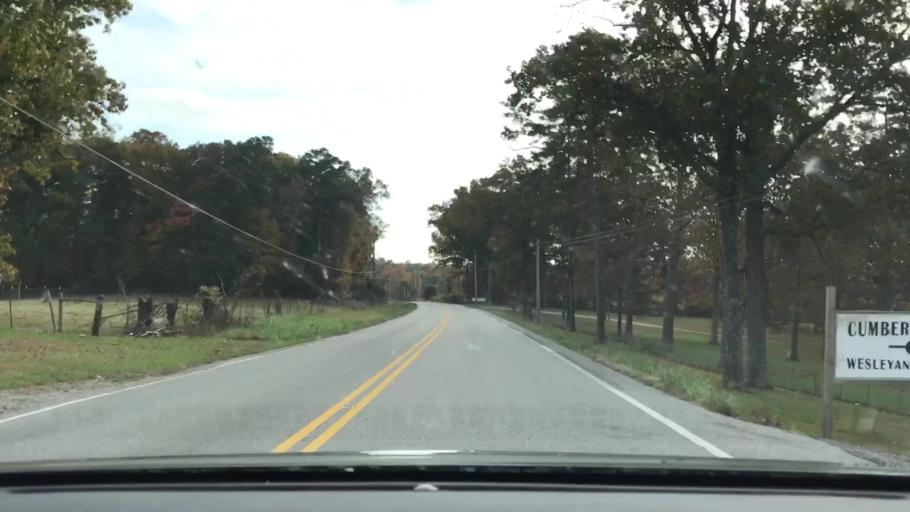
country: US
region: Tennessee
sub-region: Fentress County
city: Jamestown
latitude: 36.3844
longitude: -84.9251
